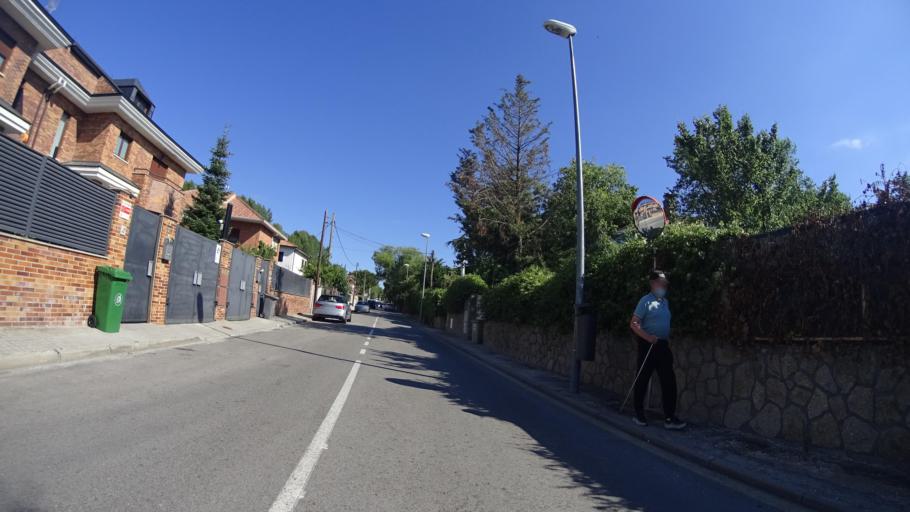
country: ES
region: Madrid
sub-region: Provincia de Madrid
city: Las Matas
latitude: 40.5459
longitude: -3.8915
